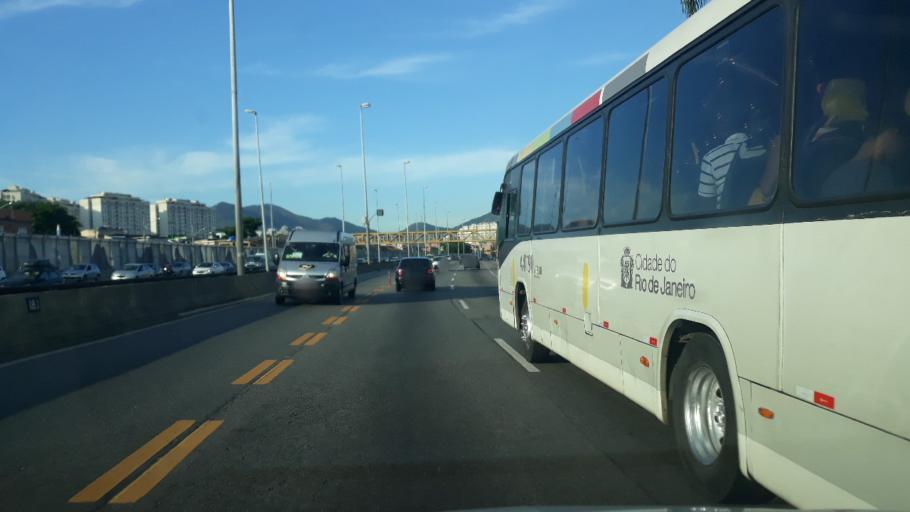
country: BR
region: Rio de Janeiro
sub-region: Rio De Janeiro
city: Rio de Janeiro
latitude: -22.8795
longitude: -43.2786
